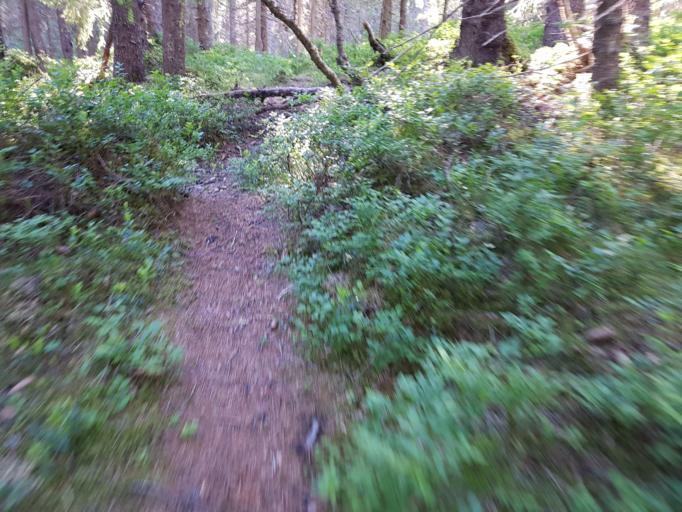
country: NO
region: Sor-Trondelag
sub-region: Trondheim
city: Trondheim
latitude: 63.4208
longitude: 10.3009
